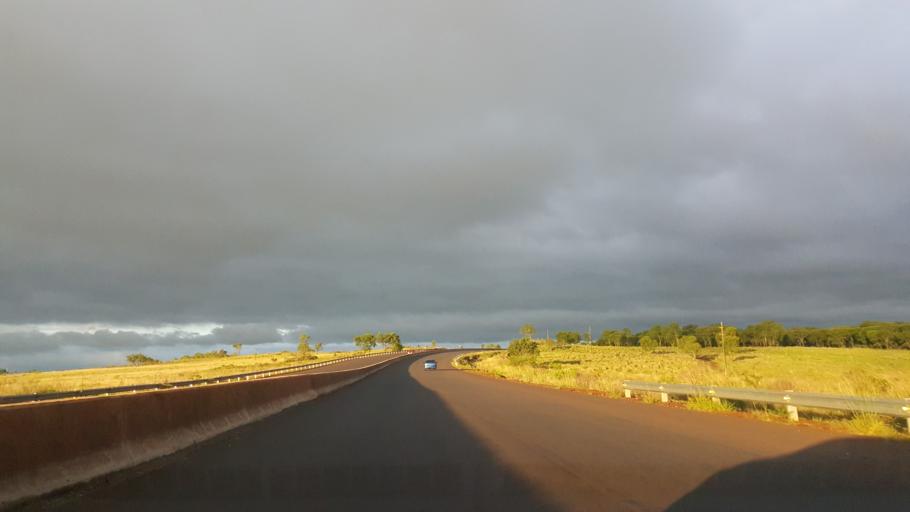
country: AR
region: Misiones
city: Cerro Cora
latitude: -27.4349
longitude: -55.6405
